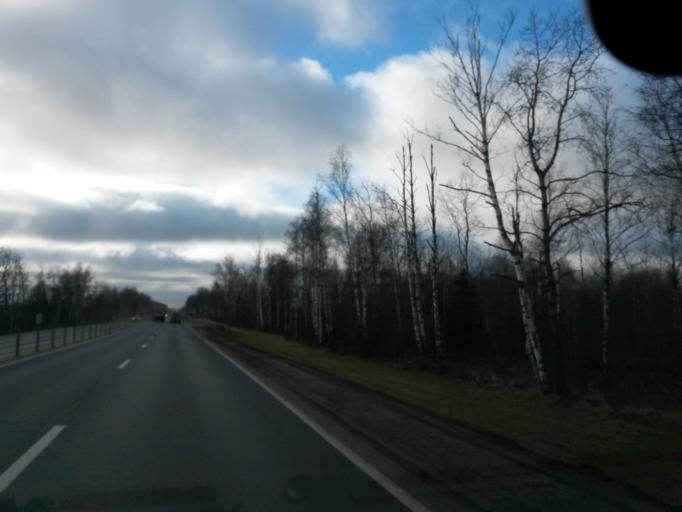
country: RU
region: Jaroslavl
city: Semibratovo
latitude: 57.3372
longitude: 39.5788
